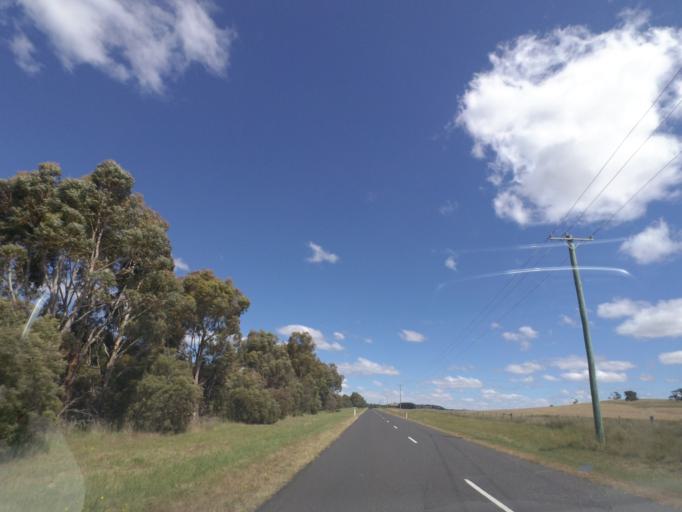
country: AU
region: Victoria
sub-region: Hume
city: Sunbury
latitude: -37.3096
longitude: 144.5170
